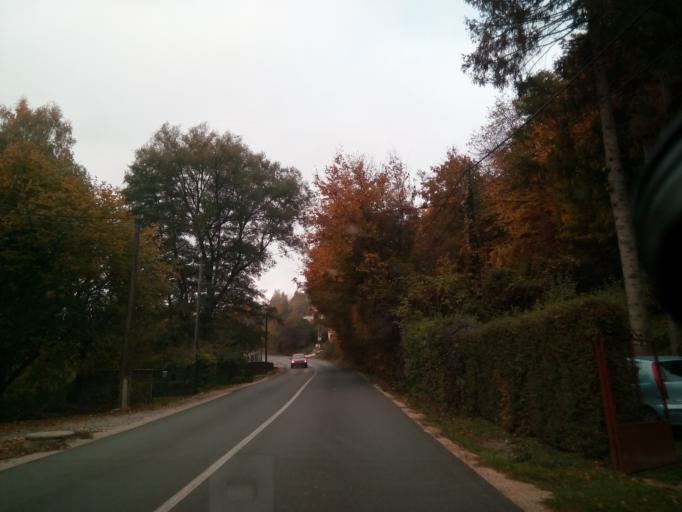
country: SK
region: Kosicky
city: Kosice
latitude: 48.7242
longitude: 21.1577
